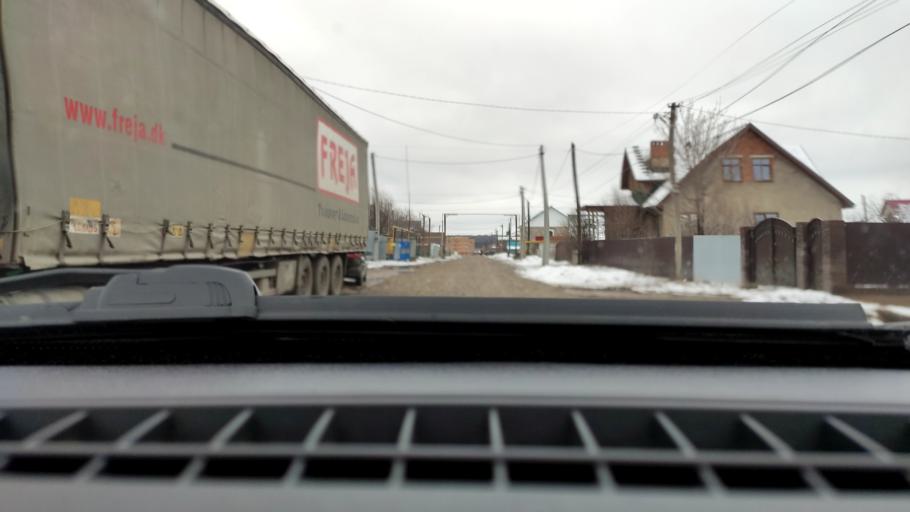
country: RU
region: Bashkortostan
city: Mikhaylovka
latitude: 54.8087
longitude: 55.7944
